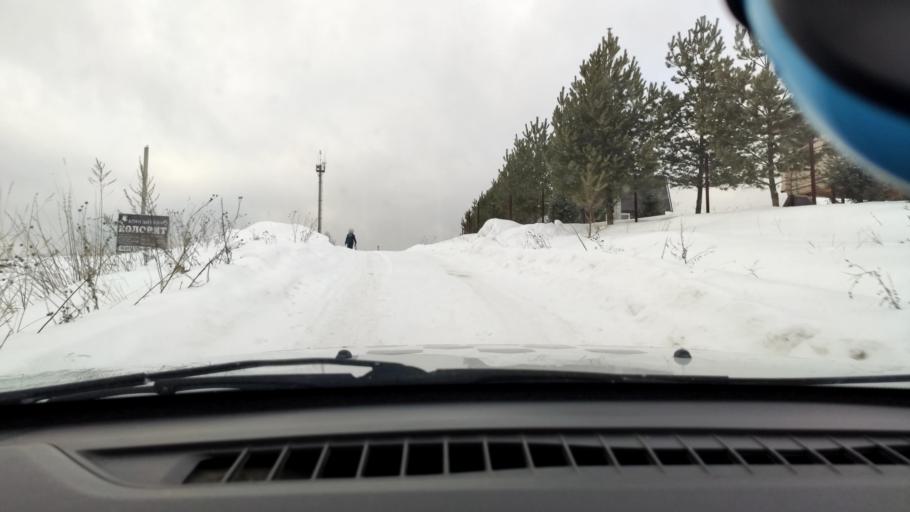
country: RU
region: Perm
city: Overyata
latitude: 58.0890
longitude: 55.9580
